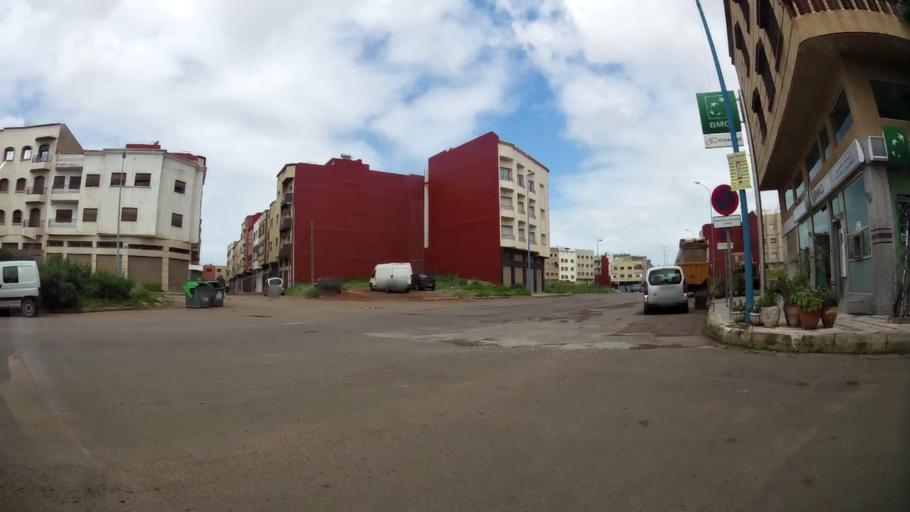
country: MA
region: Grand Casablanca
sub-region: Casablanca
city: Casablanca
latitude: 33.5350
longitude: -7.5968
